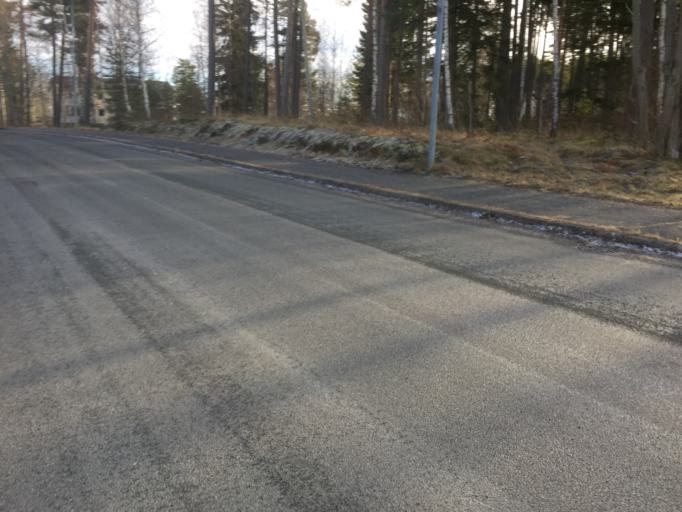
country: SE
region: Joenkoeping
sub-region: Aneby Kommun
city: Aneby
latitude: 57.8404
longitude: 14.7976
